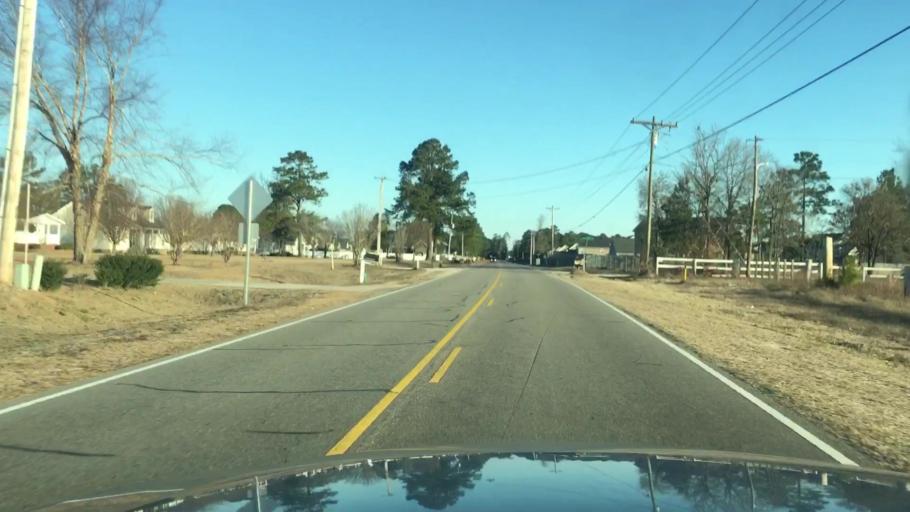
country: US
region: North Carolina
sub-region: Cumberland County
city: Hope Mills
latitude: 34.9673
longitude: -79.0078
